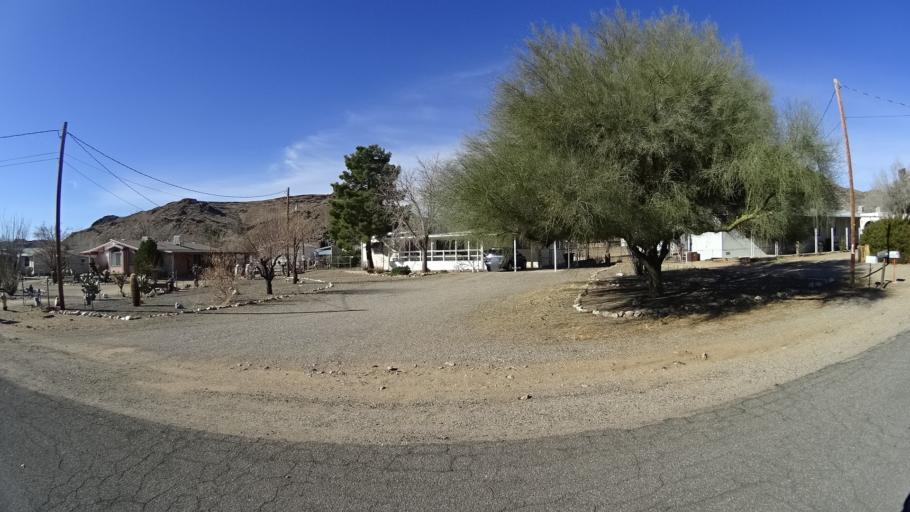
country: US
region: Arizona
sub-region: Mohave County
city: New Kingman-Butler
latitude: 35.2698
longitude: -114.0451
